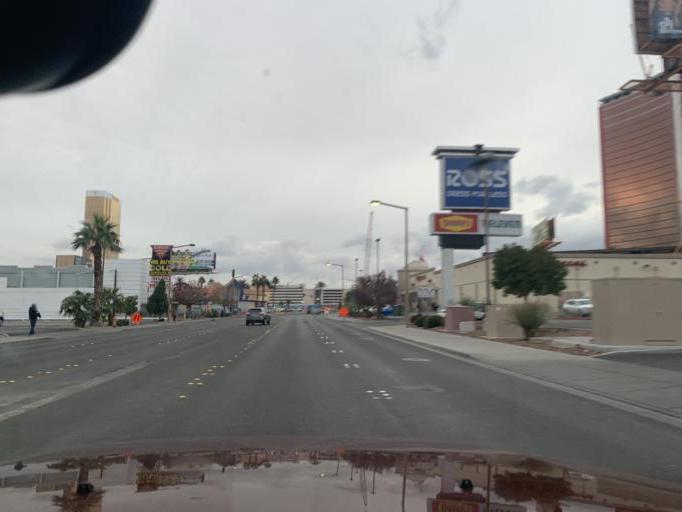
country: US
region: Nevada
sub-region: Clark County
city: Paradise
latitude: 36.1324
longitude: -115.1626
